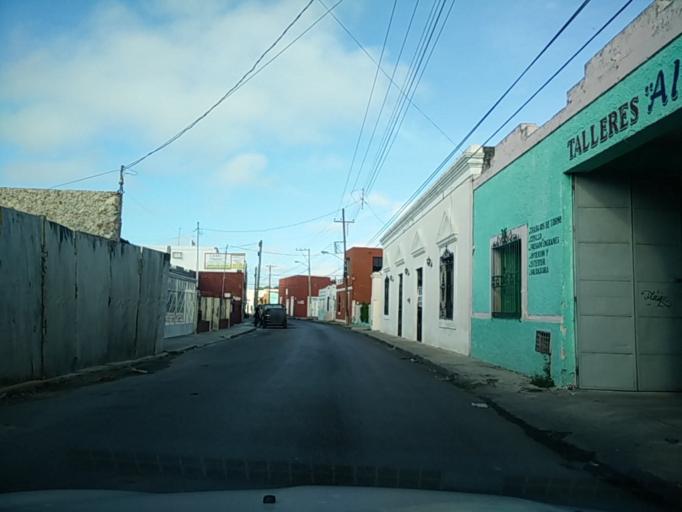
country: MX
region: Yucatan
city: Merida
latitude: 20.9674
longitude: -89.6350
